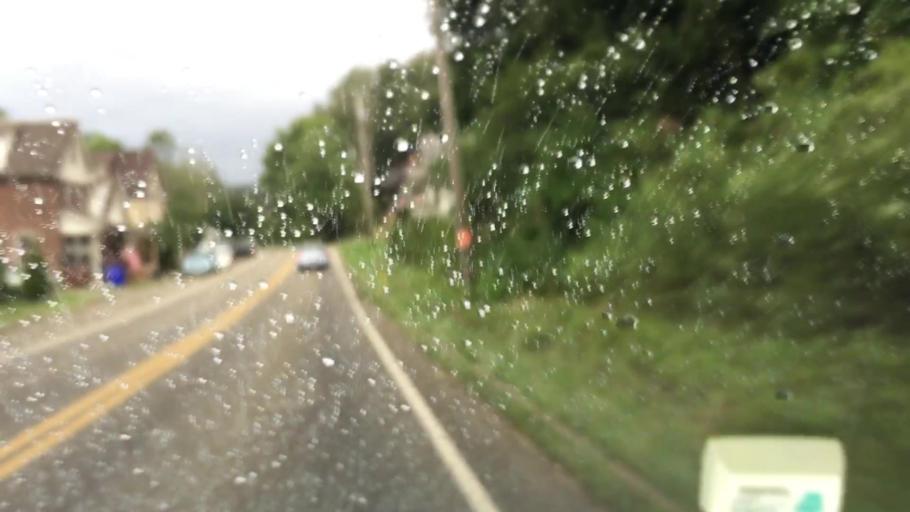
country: US
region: Pennsylvania
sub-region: Butler County
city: Homeacre-Lyndora
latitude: 40.8535
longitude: -79.9182
